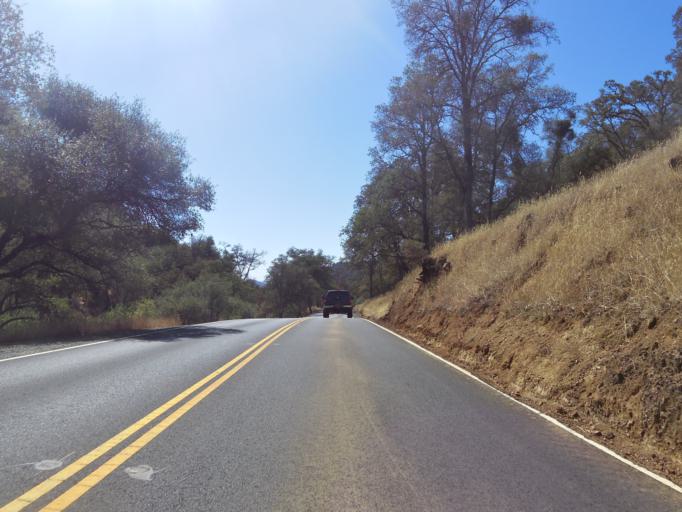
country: US
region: California
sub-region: El Dorado County
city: Deer Park
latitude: 38.6107
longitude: -120.8528
